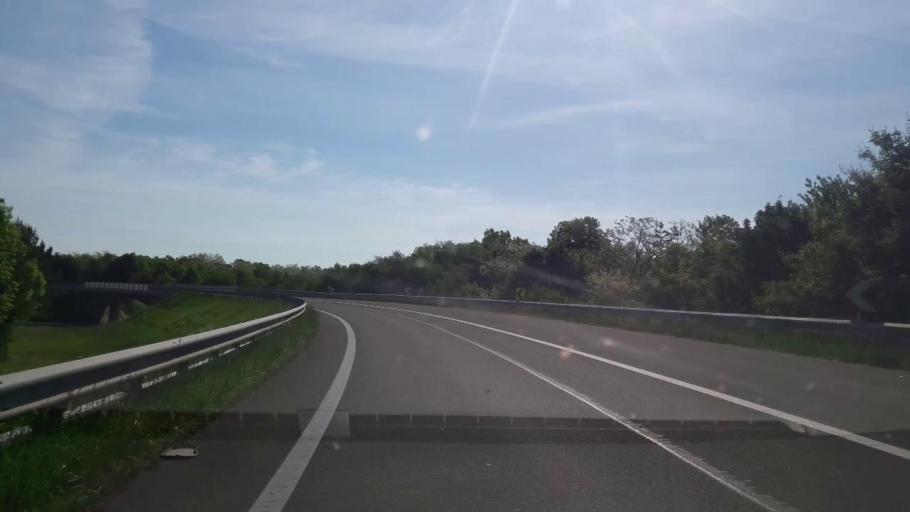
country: AT
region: Burgenland
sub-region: Eisenstadt-Umgebung
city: Wulkaprodersdorf
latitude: 47.8135
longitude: 16.4954
